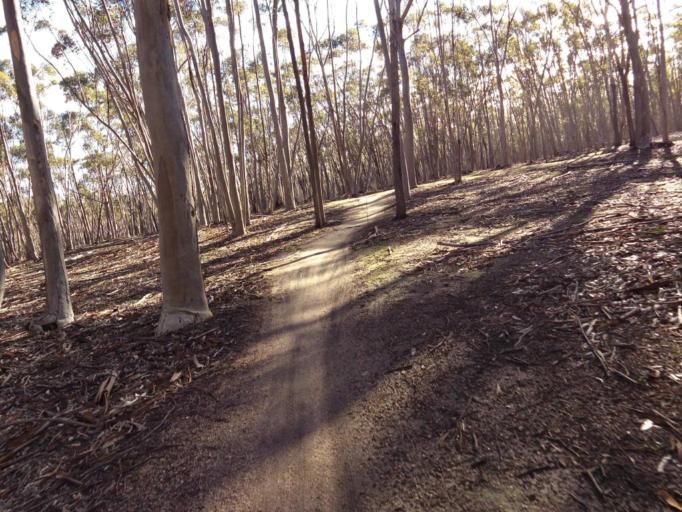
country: AU
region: Victoria
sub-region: Greater Geelong
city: Lara
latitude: -37.9632
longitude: 144.4069
